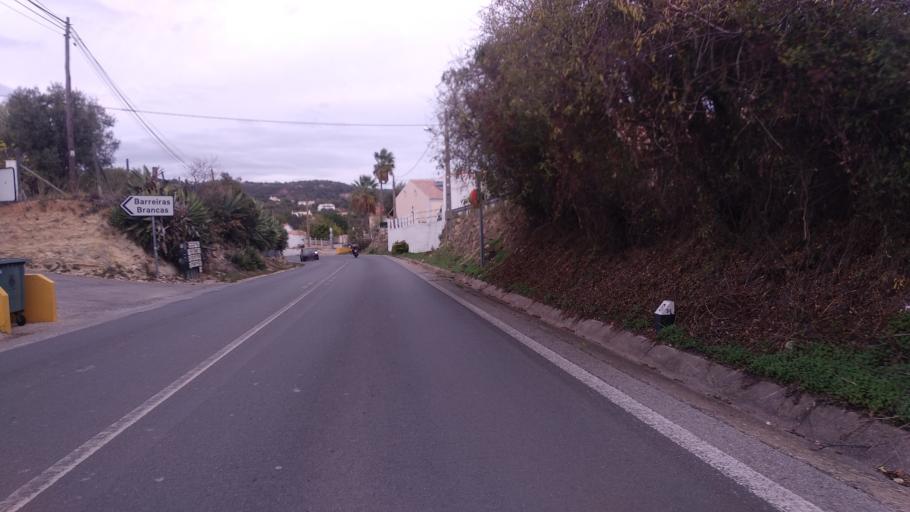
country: PT
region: Faro
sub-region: Loule
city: Loule
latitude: 37.1423
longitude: -7.9818
